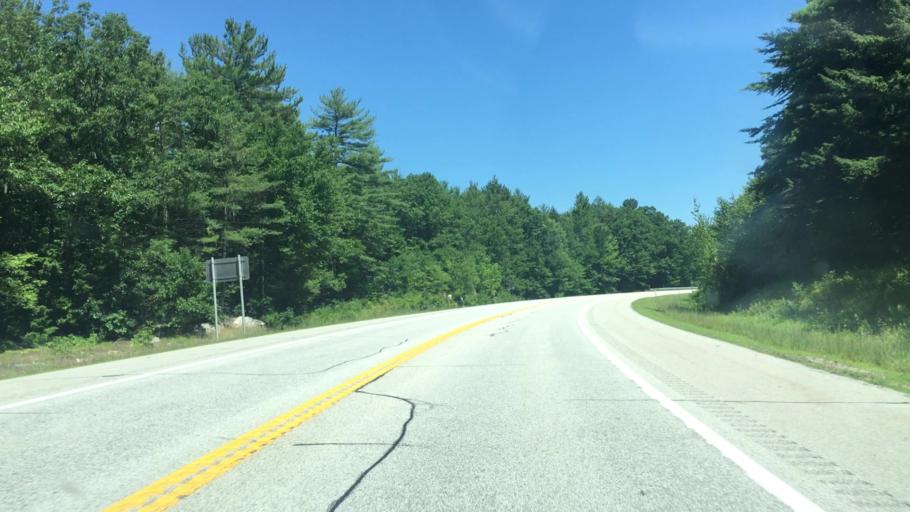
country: US
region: New Hampshire
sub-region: Merrimack County
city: Contoocook
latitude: 43.1806
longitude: -71.7371
